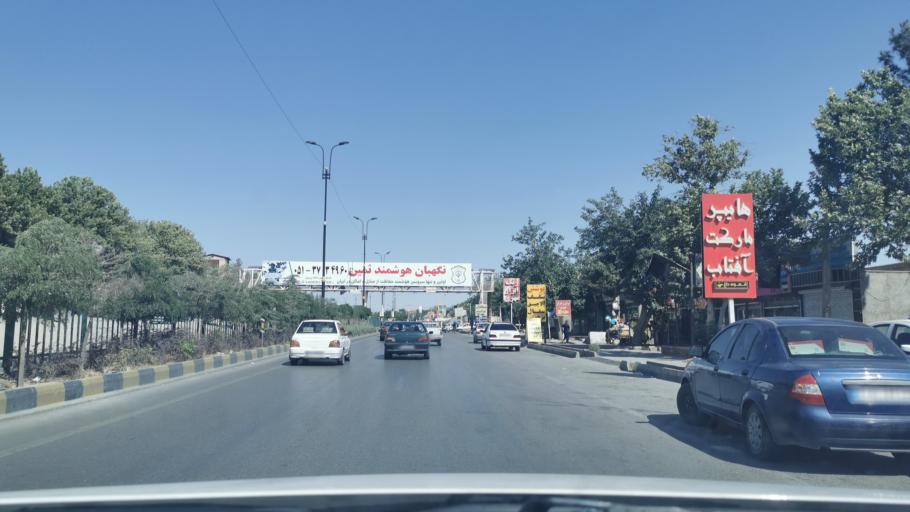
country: IR
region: Razavi Khorasan
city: Torqabeh
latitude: 36.4008
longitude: 59.3891
